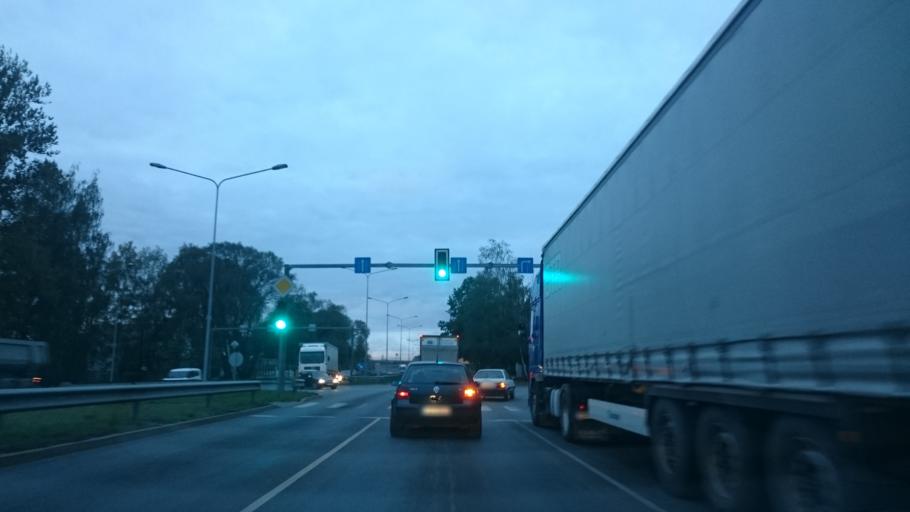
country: LV
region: Riga
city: Riga
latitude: 56.9256
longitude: 24.1880
